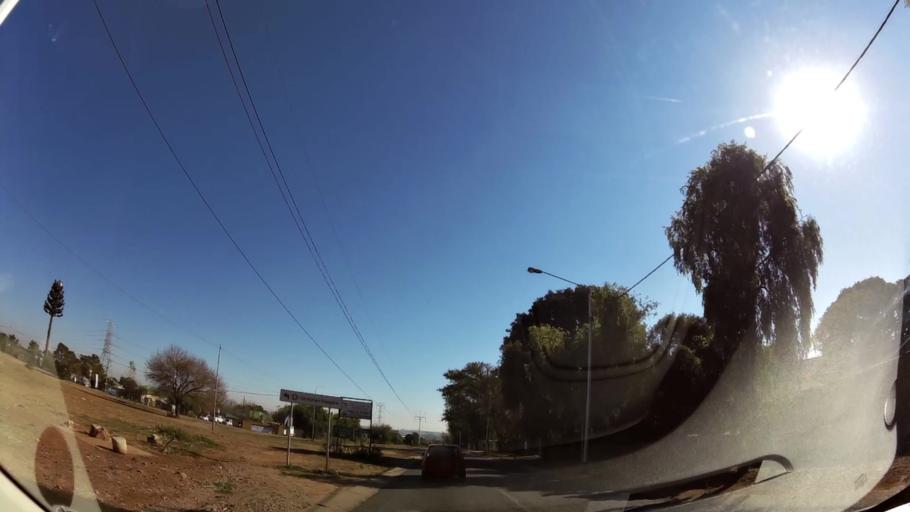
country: ZA
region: Gauteng
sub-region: City of Tshwane Metropolitan Municipality
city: Centurion
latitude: -25.8284
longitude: 28.1954
